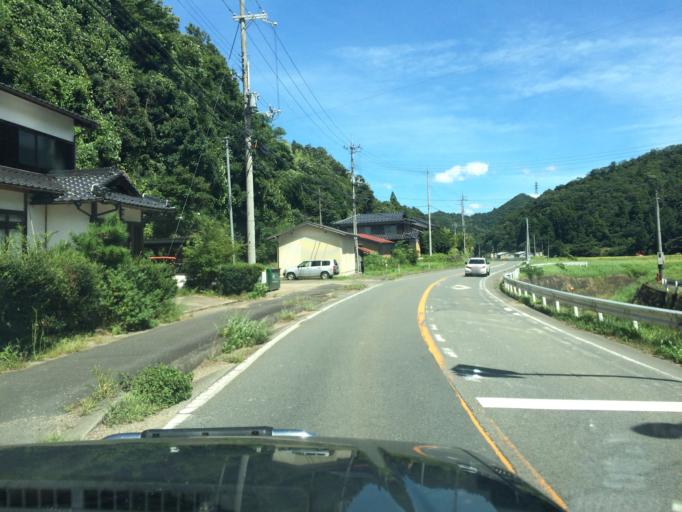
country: JP
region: Hyogo
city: Toyooka
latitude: 35.4566
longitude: 134.8258
